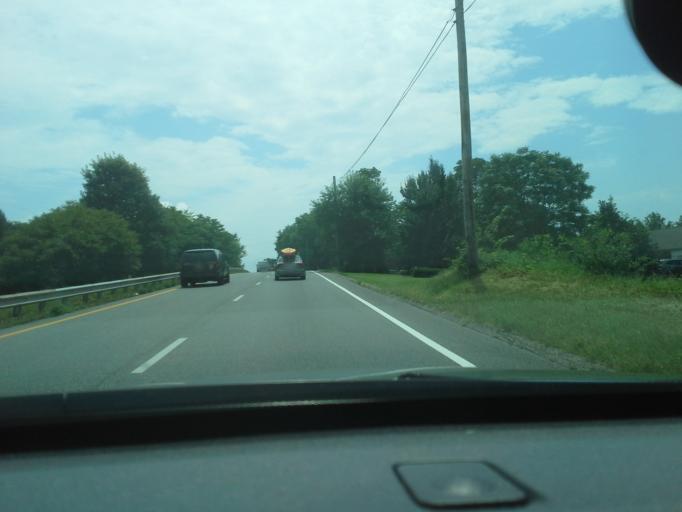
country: US
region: Maryland
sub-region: Calvert County
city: Dunkirk Town Center
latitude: 38.7036
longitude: -76.6476
